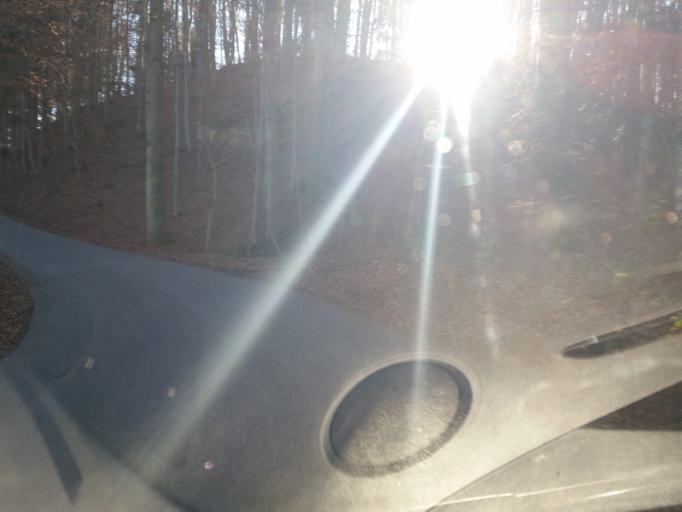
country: CH
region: Aargau
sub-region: Bezirk Bremgarten
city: Rudolfstetten
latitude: 47.3888
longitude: 8.3742
